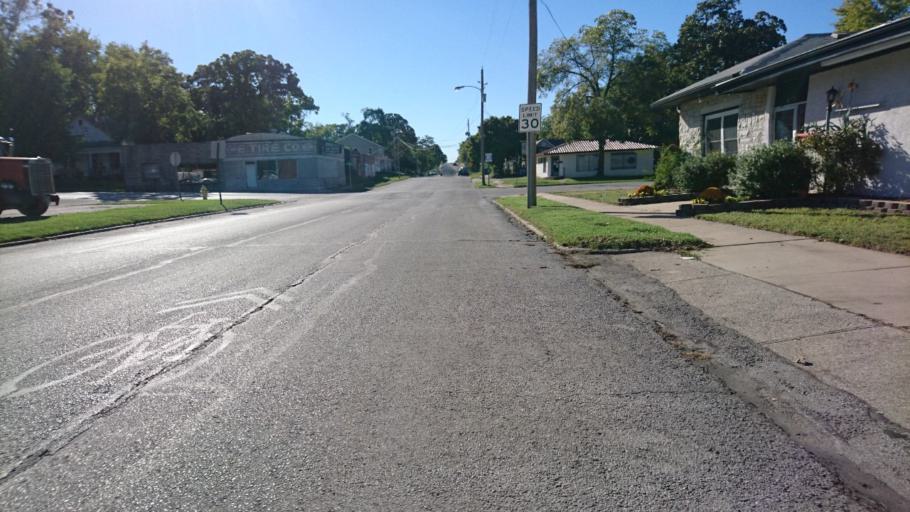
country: US
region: Missouri
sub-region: Jasper County
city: Carthage
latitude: 37.1764
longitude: -94.3152
